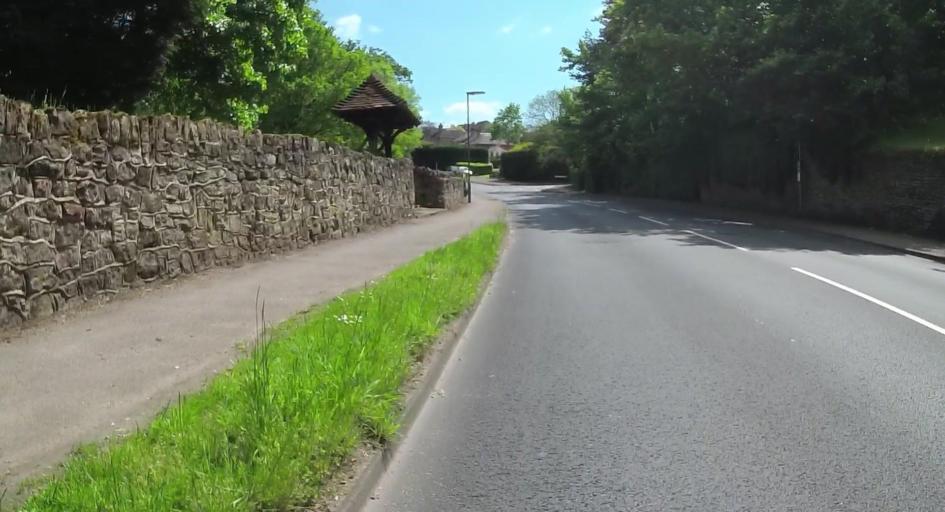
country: GB
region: England
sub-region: Surrey
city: Farnham
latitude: 51.1979
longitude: -0.8173
